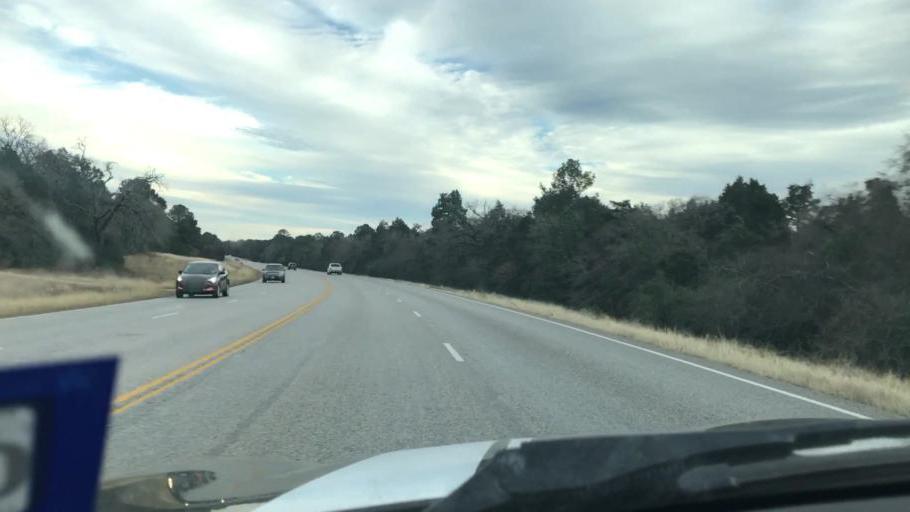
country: US
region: Texas
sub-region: Bastrop County
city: Camp Swift
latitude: 30.2473
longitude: -97.2222
